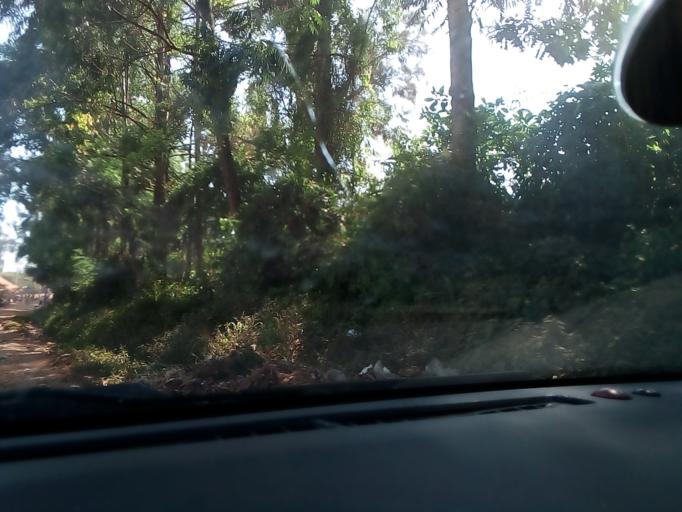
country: UG
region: Central Region
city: Masaka
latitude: -0.3509
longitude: 31.7353
